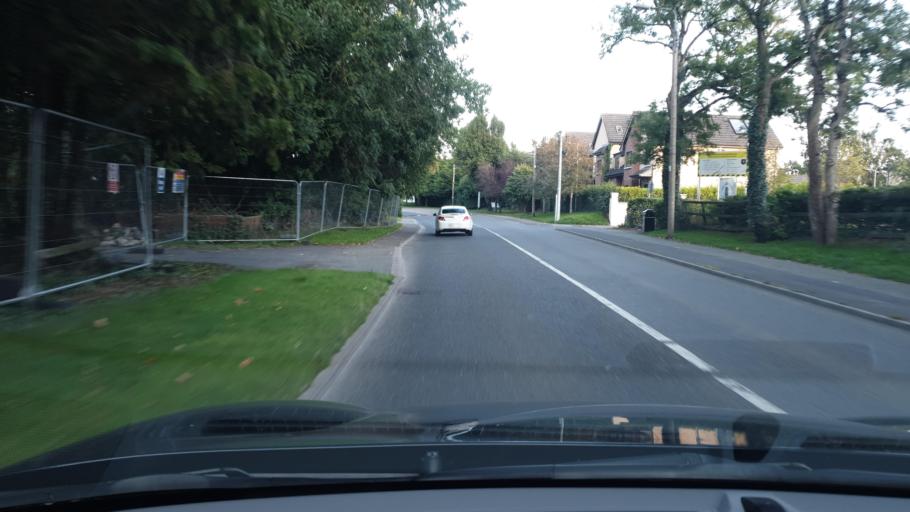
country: IE
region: Leinster
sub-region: Kildare
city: Kill
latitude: 53.2462
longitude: -6.5982
